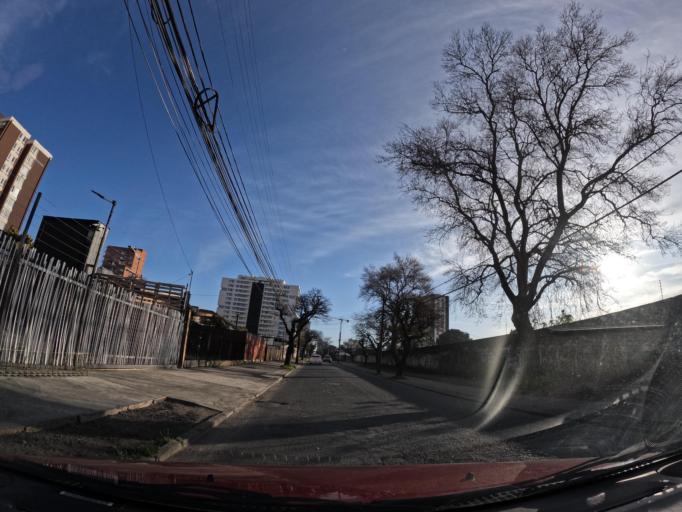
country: CL
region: Biobio
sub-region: Provincia de Concepcion
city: Concepcion
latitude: -36.8159
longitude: -73.0375
